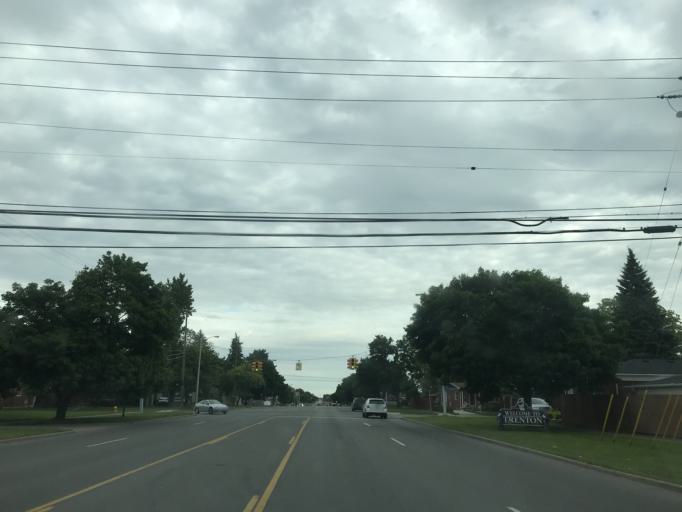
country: US
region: Michigan
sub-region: Wayne County
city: Woodhaven
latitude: 42.1410
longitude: -83.2168
